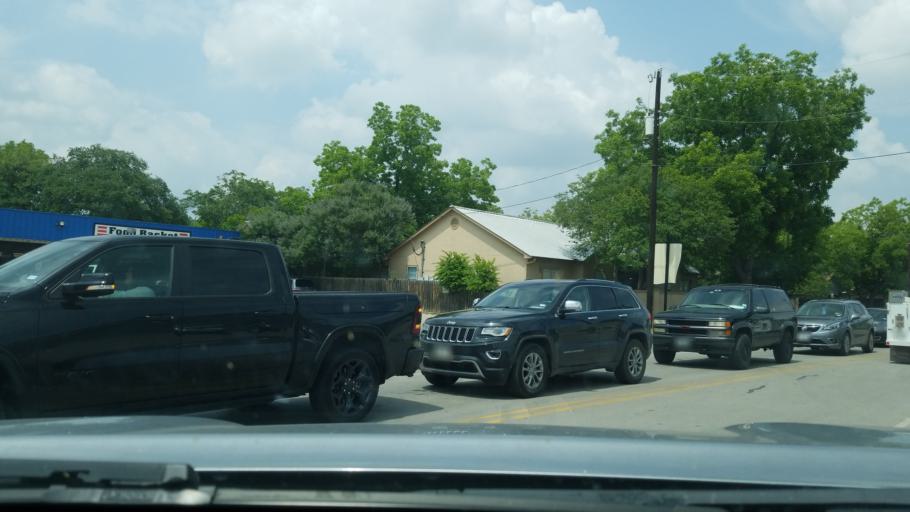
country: US
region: Texas
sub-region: Comal County
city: New Braunfels
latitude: 29.7099
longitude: -98.1196
